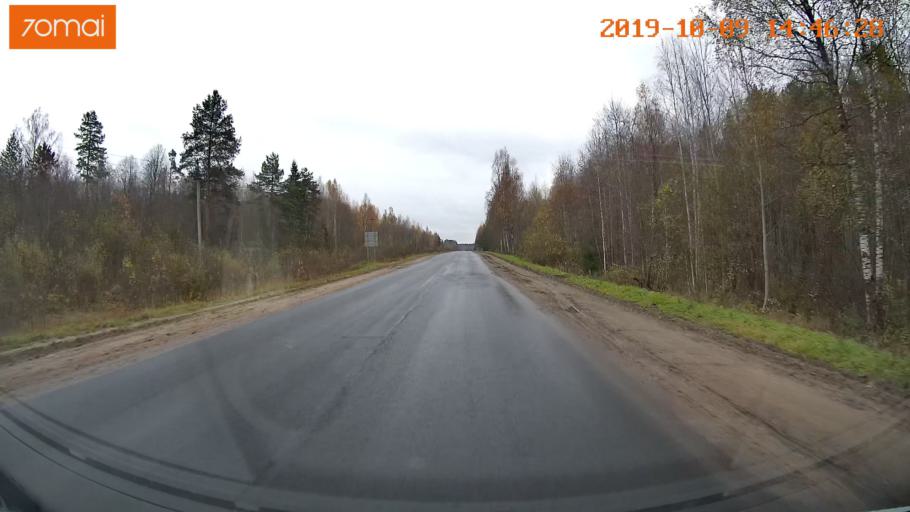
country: RU
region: Kostroma
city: Buy
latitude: 58.4310
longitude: 41.5767
